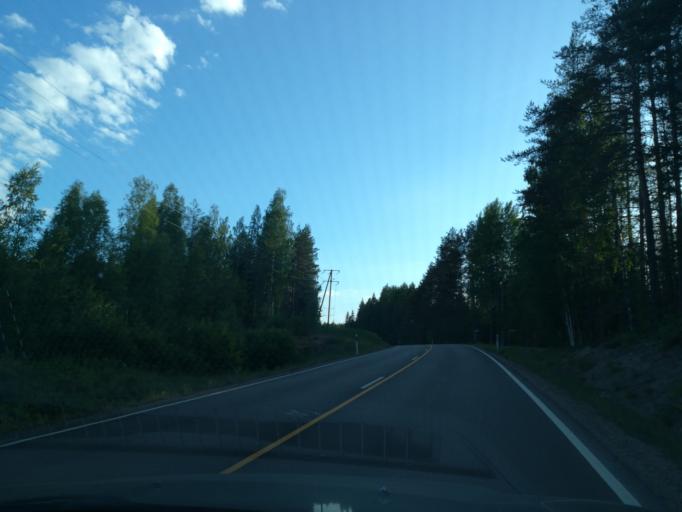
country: FI
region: Southern Savonia
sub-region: Mikkeli
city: Puumala
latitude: 61.5782
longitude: 28.1645
